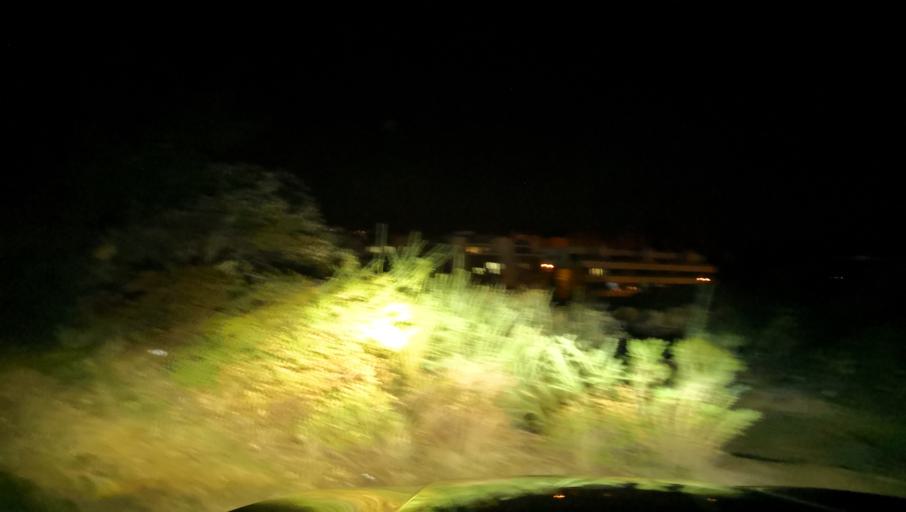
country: PT
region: Vila Real
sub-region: Vila Real
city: Vila Real
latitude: 41.3086
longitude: -7.7291
